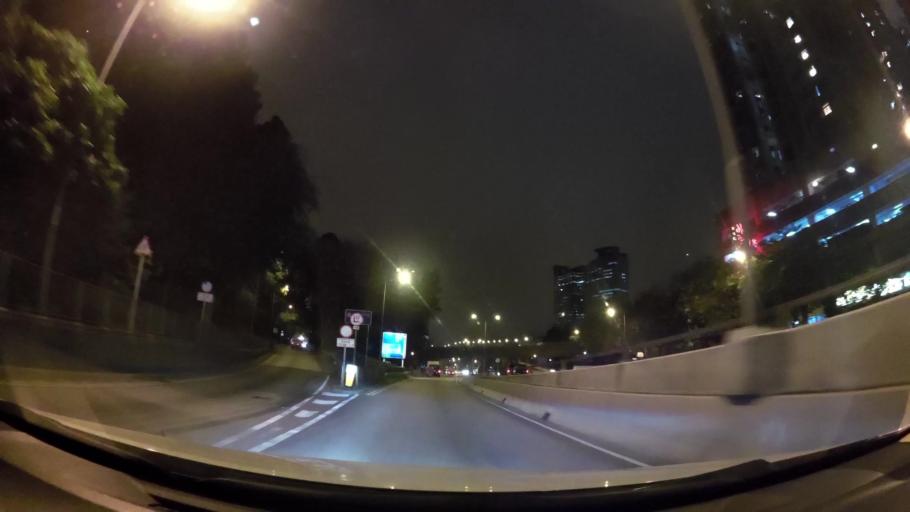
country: HK
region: Tsuen Wan
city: Tsuen Wan
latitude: 22.3551
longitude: 114.1290
